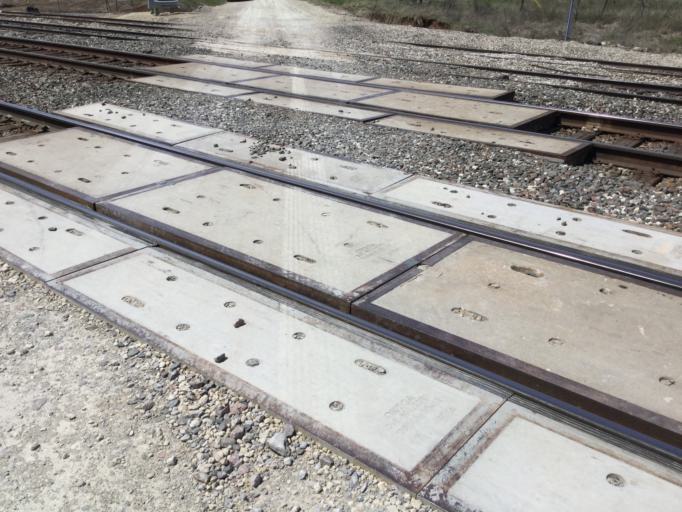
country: US
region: Kansas
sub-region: Butler County
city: Augusta
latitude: 37.6938
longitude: -96.9525
